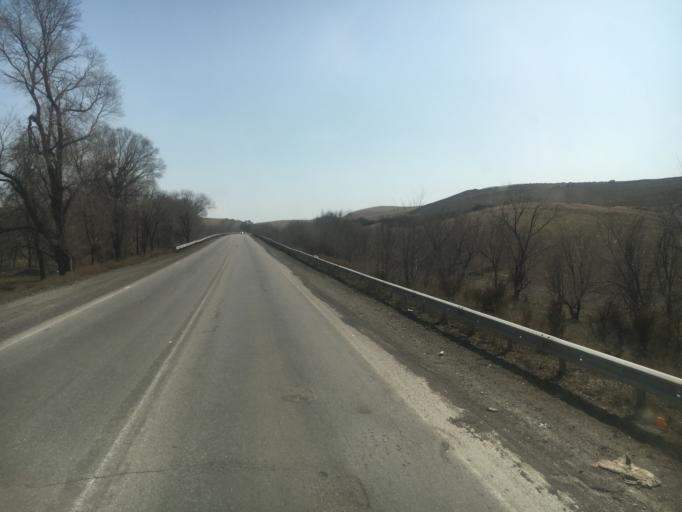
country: KZ
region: Almaty Oblysy
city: Burunday
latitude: 43.2963
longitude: 76.2311
